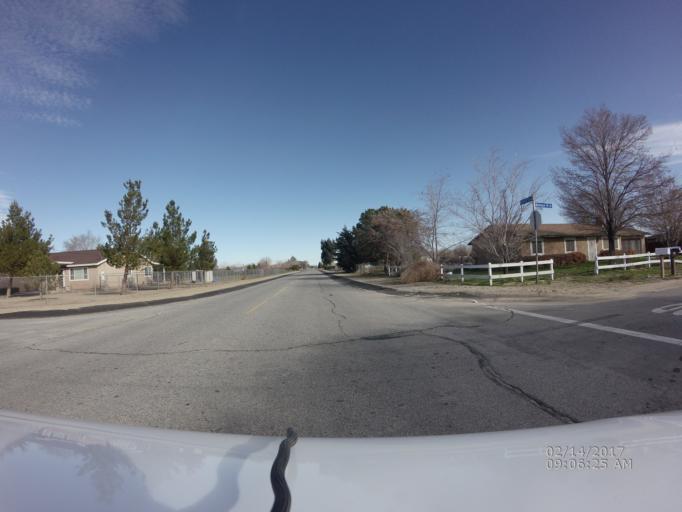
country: US
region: California
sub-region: Los Angeles County
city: Littlerock
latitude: 34.5671
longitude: -117.9431
